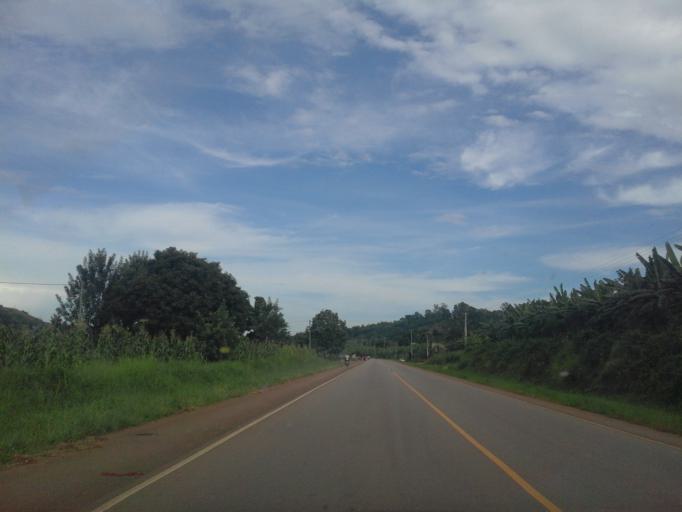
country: UG
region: Central Region
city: Masaka
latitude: -0.3425
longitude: 31.6310
